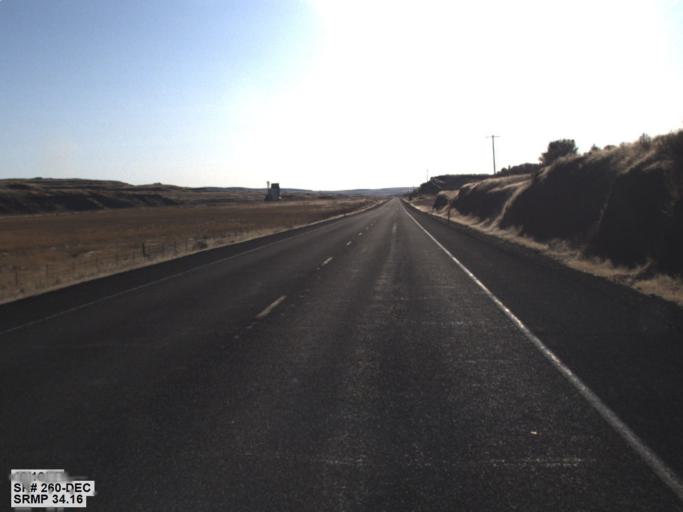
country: US
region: Washington
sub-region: Adams County
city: Ritzville
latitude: 46.7110
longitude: -118.3940
